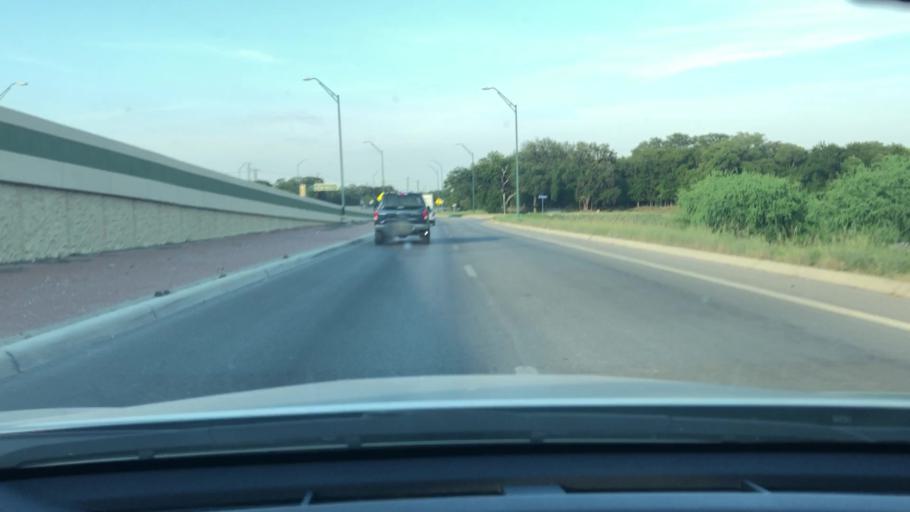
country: US
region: Texas
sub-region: Bexar County
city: Alamo Heights
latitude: 29.5459
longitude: -98.4530
